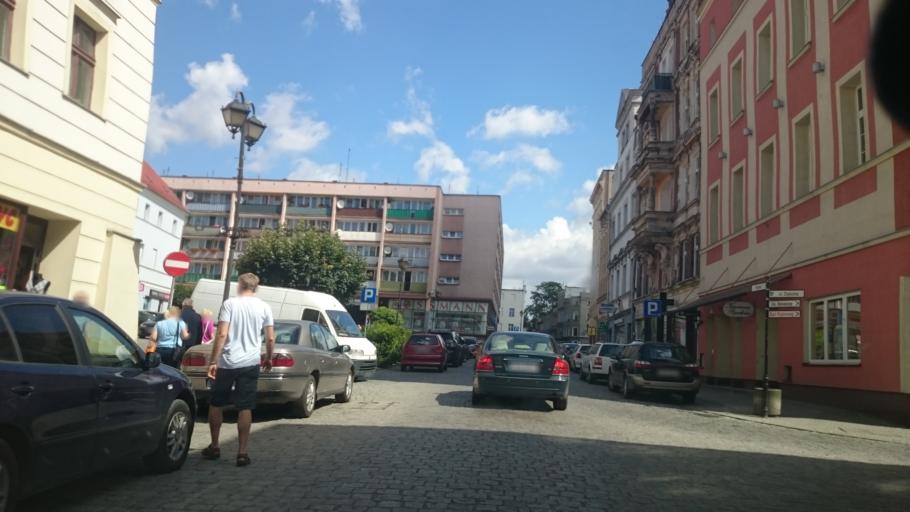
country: PL
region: Lower Silesian Voivodeship
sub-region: Powiat zabkowicki
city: Zabkowice Slaskie
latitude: 50.5891
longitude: 16.8121
